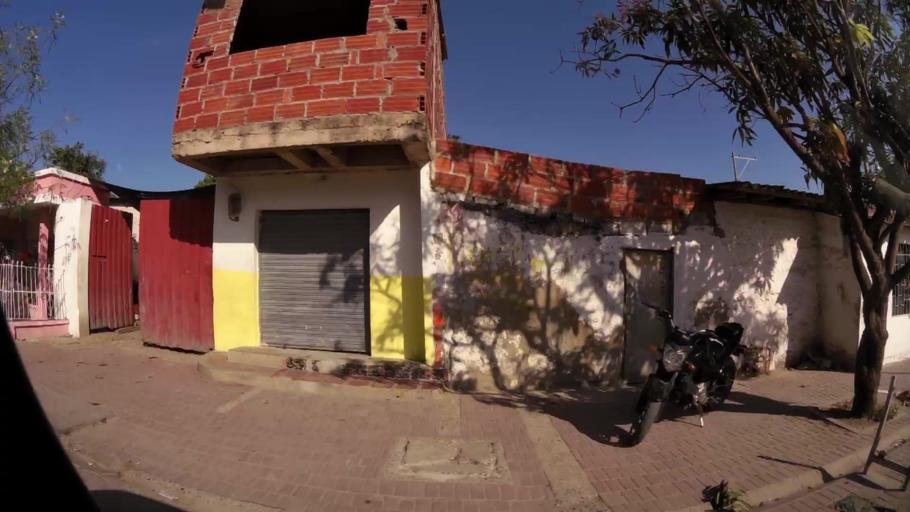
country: CO
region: Bolivar
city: Cartagena
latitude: 10.4094
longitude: -75.4964
